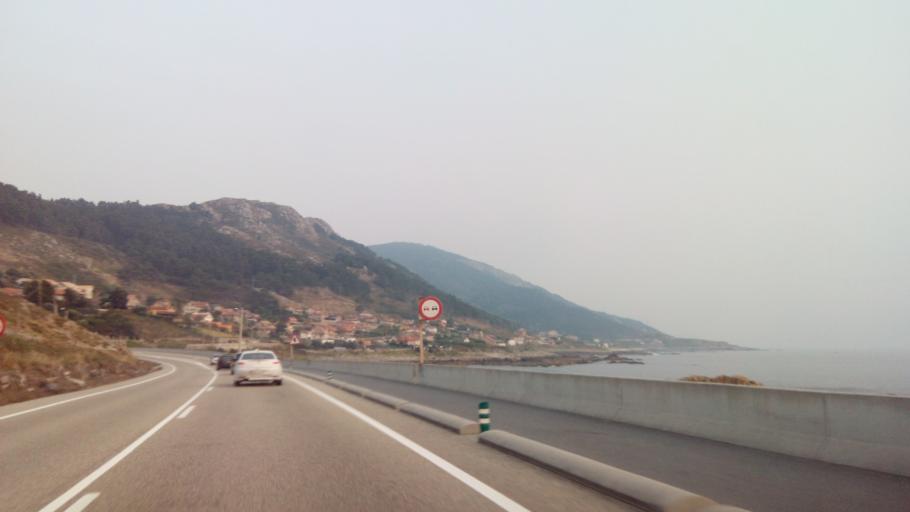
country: ES
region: Galicia
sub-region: Provincia de Pontevedra
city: Baiona
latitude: 42.1025
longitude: -8.8971
